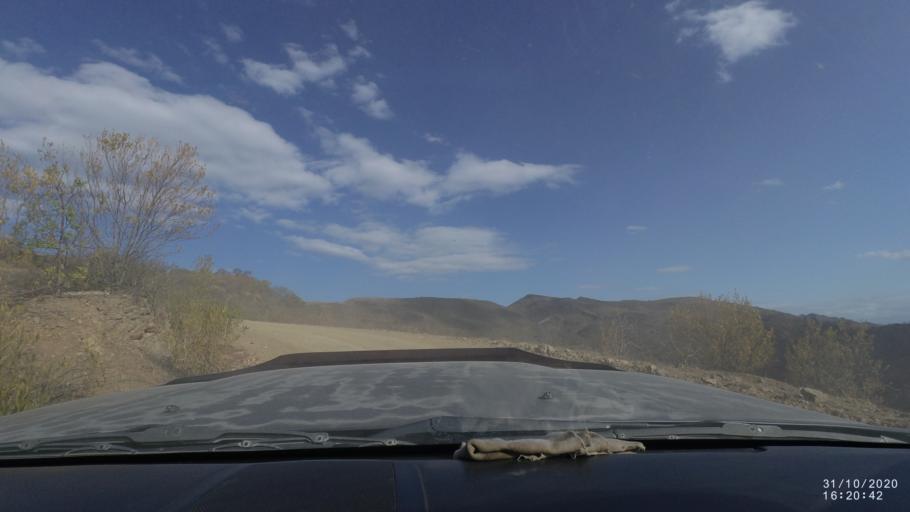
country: BO
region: Chuquisaca
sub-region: Provincia Zudanez
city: Mojocoya
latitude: -18.3979
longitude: -64.6005
